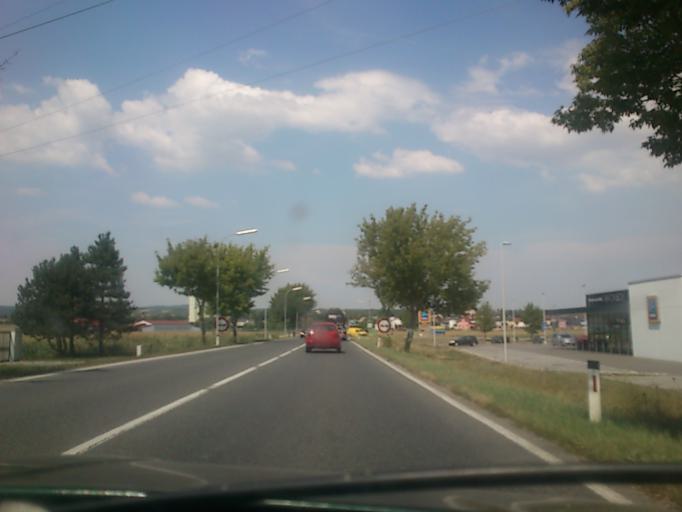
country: AT
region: Lower Austria
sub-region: Politischer Bezirk Mistelbach
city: Poysdorf
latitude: 48.6551
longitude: 16.6310
